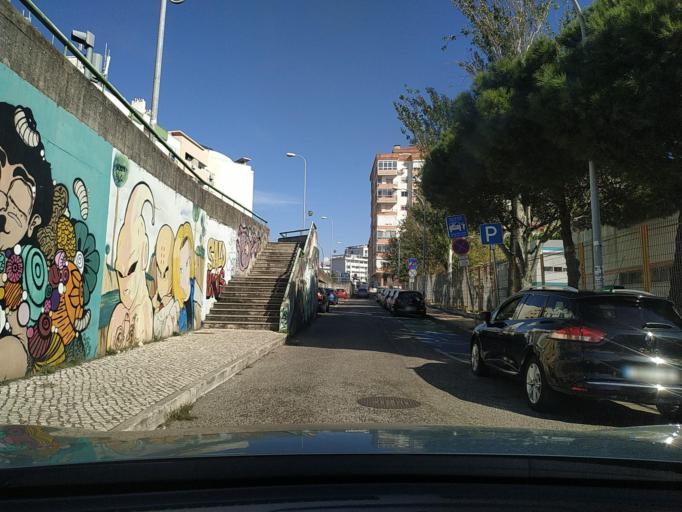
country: PT
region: Lisbon
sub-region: Sintra
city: Queluz
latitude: 38.7608
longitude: -9.2469
